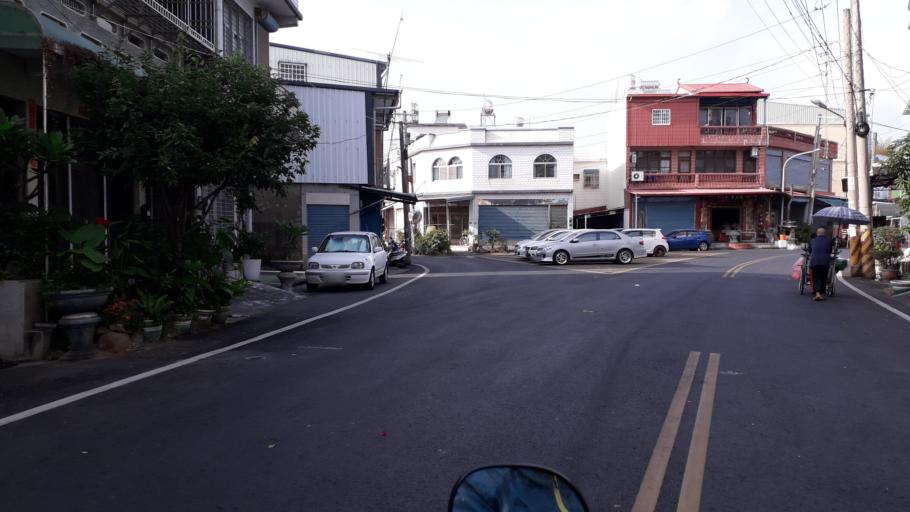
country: TW
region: Taiwan
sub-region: Pingtung
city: Pingtung
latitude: 22.3596
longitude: 120.5992
